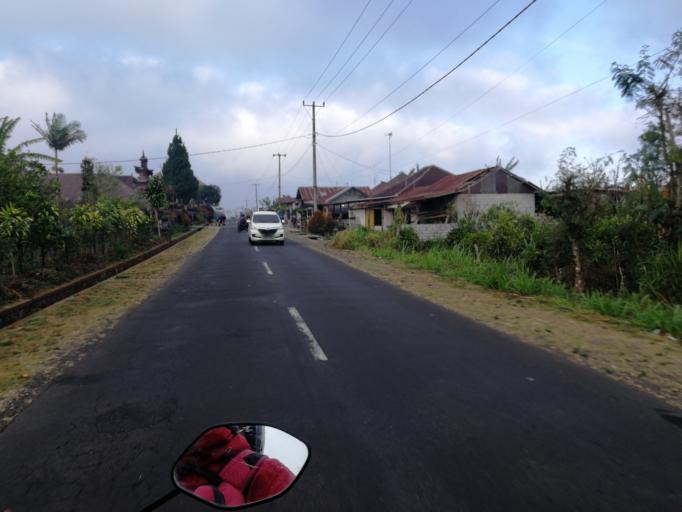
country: ID
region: Bali
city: Banjar Kedisan
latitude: -8.2220
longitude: 115.2660
